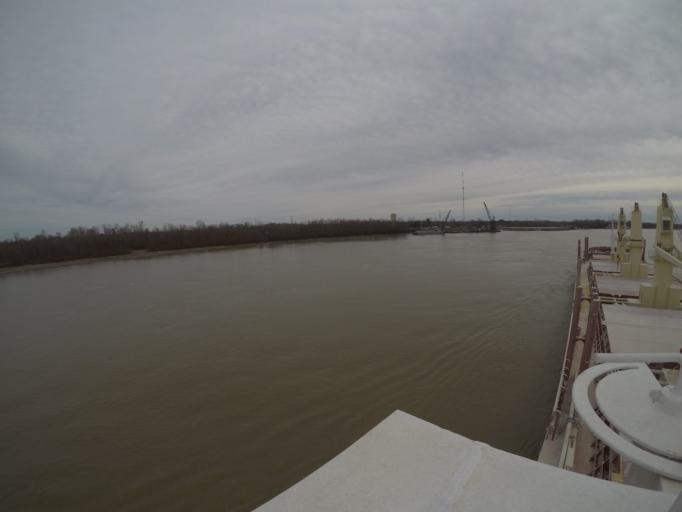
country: US
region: Louisiana
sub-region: Saint John the Baptist Parish
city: Laplace
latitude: 30.0508
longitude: -90.4828
